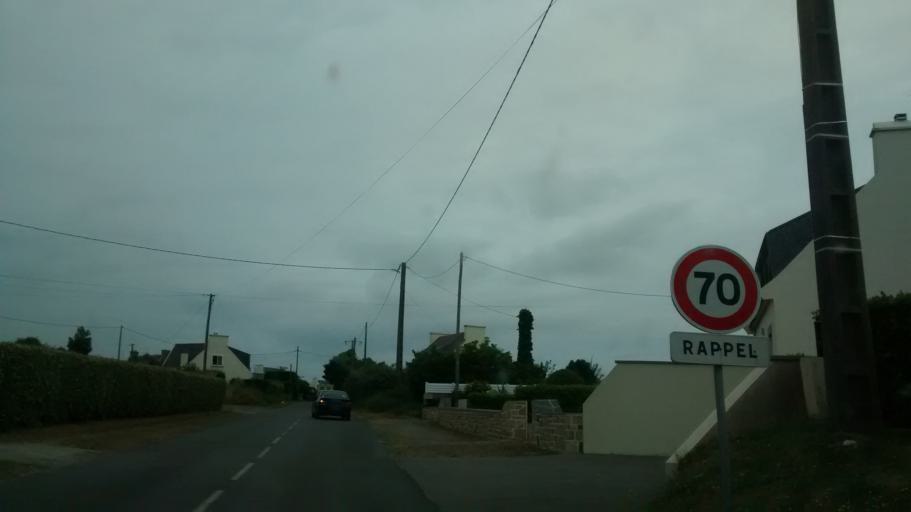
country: FR
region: Brittany
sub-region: Departement du Finistere
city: Guisseny
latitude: 48.6352
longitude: -4.4298
